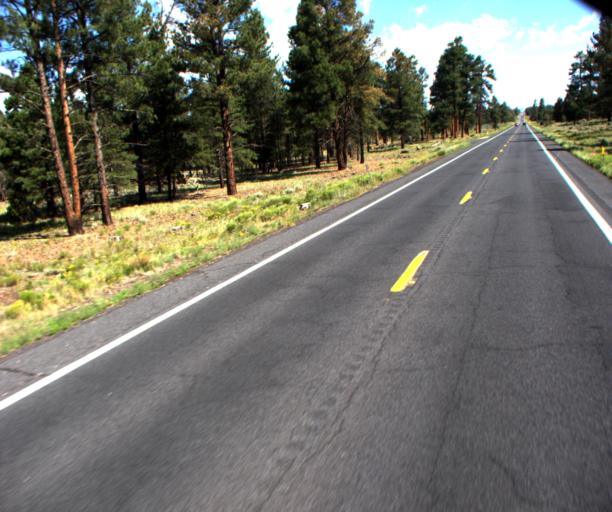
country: US
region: Arizona
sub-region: Coconino County
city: Grand Canyon Village
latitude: 35.9165
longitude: -112.1299
